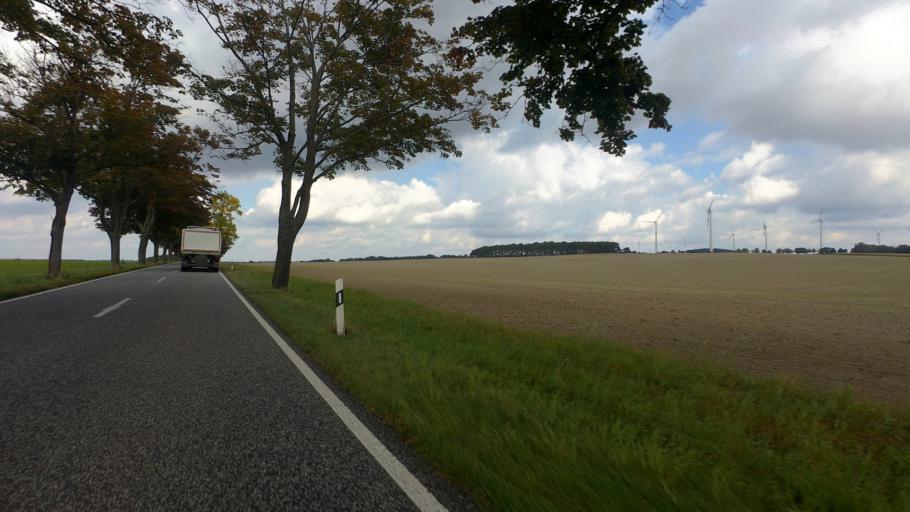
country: DE
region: Brandenburg
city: Juterbog
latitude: 51.9602
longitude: 13.1115
